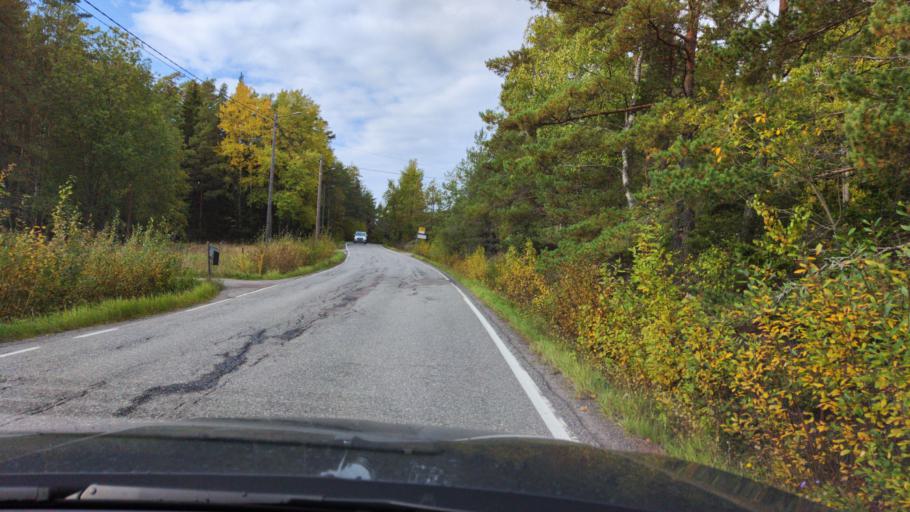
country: FI
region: Varsinais-Suomi
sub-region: Aboland-Turunmaa
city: Pargas
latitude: 60.3538
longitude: 22.1787
